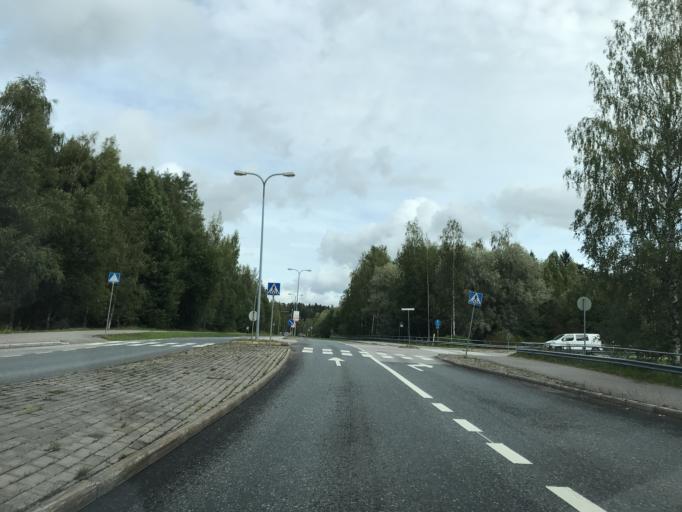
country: FI
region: Paijanne Tavastia
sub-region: Lahti
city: Lahti
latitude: 60.9924
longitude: 25.7463
